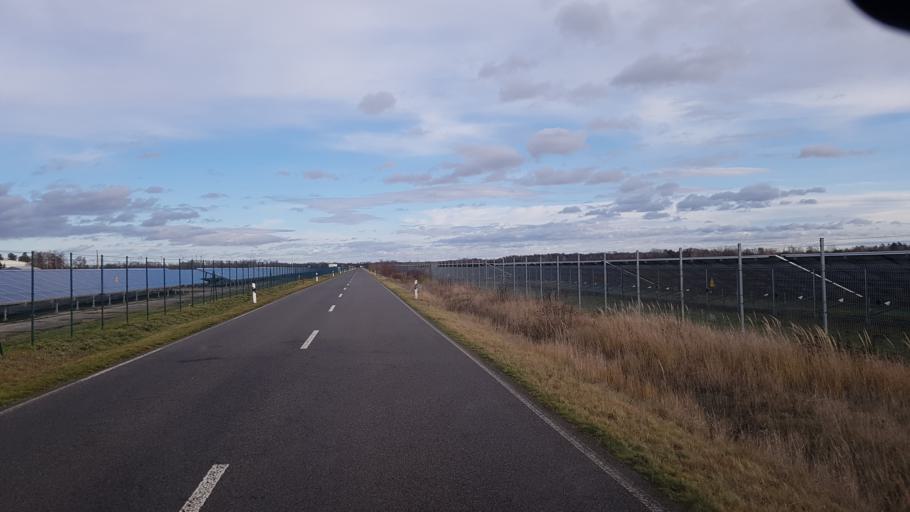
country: DE
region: Brandenburg
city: Falkenberg
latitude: 51.5475
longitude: 13.2104
